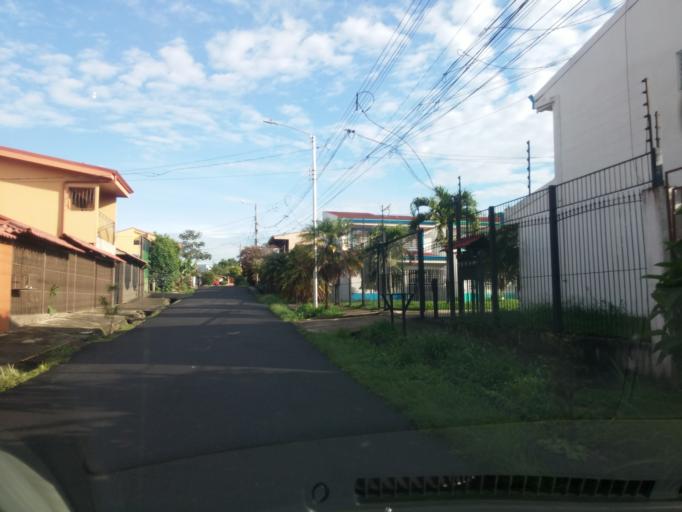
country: CR
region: Heredia
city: Llorente
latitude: 9.9978
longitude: -84.1515
